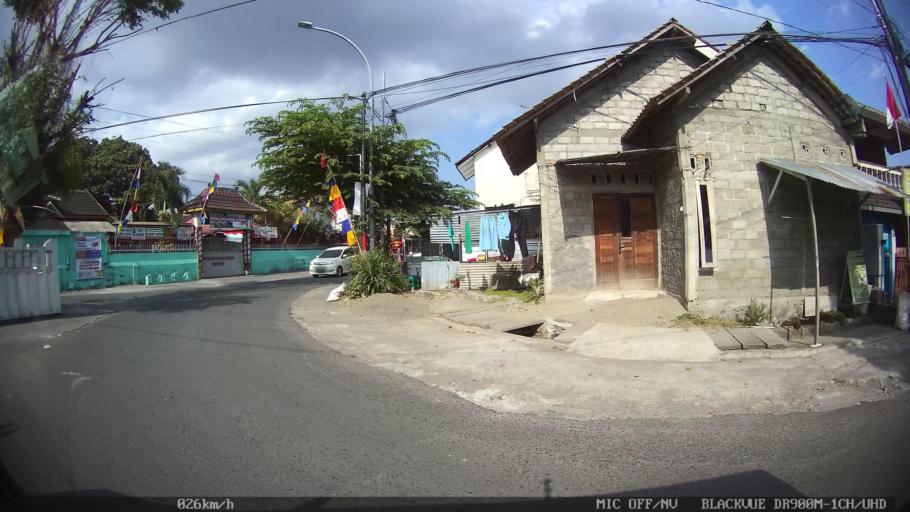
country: ID
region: Daerah Istimewa Yogyakarta
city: Yogyakarta
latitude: -7.7940
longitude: 110.3461
